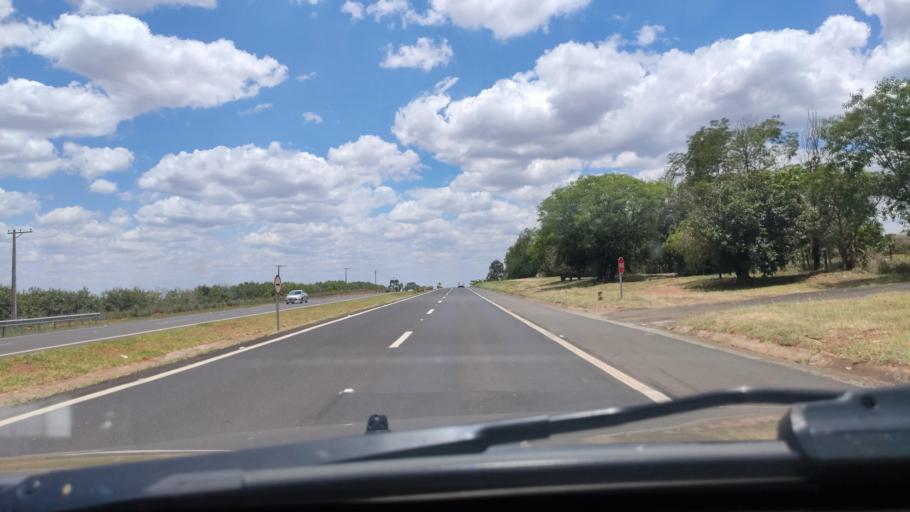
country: BR
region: Sao Paulo
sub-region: Duartina
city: Duartina
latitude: -22.6495
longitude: -49.4054
